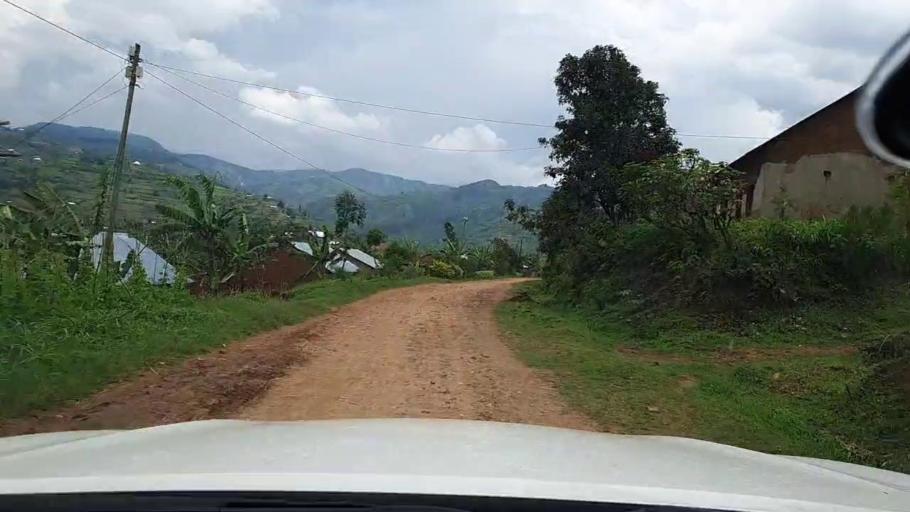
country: RW
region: Western Province
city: Kibuye
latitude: -2.0719
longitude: 29.4257
